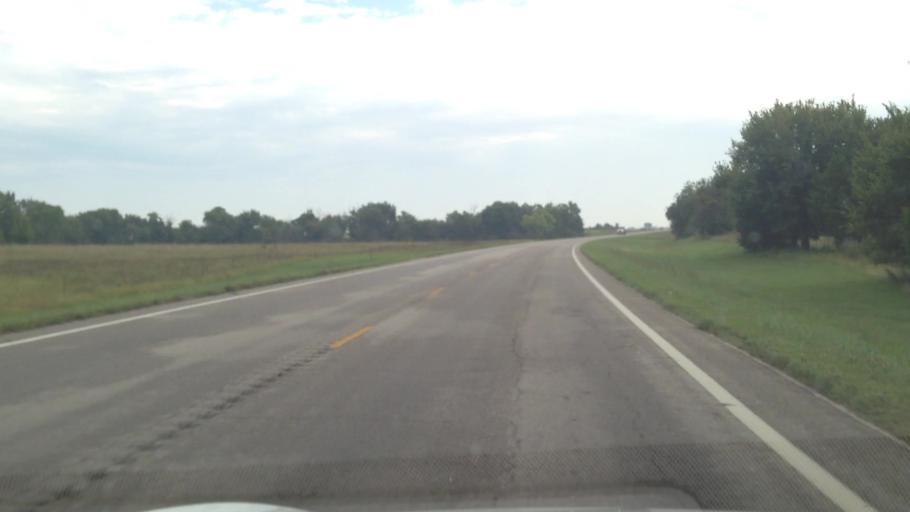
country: US
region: Kansas
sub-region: Bourbon County
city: Fort Scott
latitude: 37.8917
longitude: -95.0396
